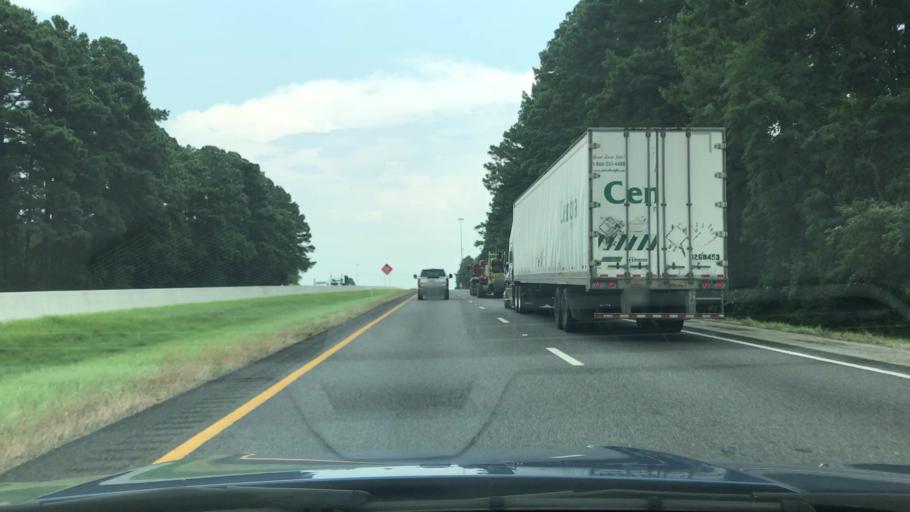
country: US
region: Texas
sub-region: Gregg County
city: Liberty City
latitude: 32.4347
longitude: -94.9534
